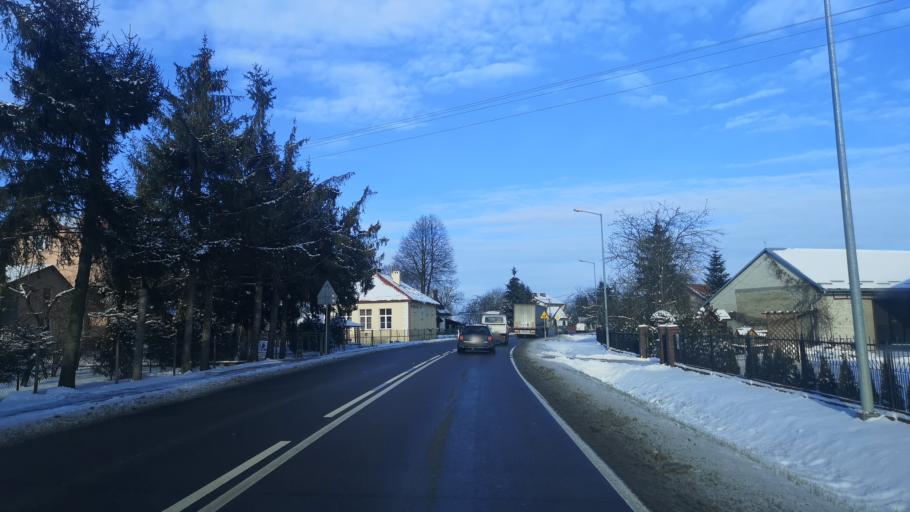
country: PL
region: Subcarpathian Voivodeship
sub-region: Powiat przeworski
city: Tryncza
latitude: 50.1353
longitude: 22.5370
